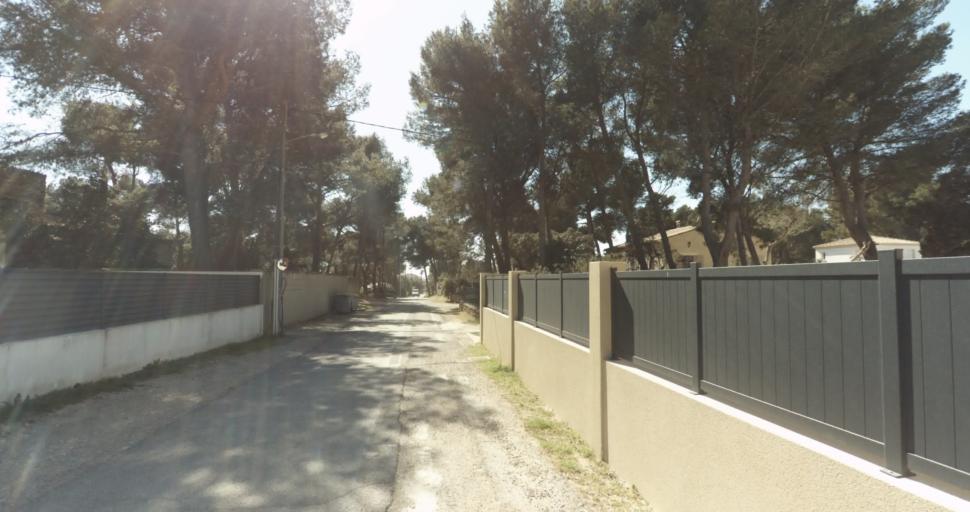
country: FR
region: Provence-Alpes-Cote d'Azur
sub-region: Departement des Bouches-du-Rhone
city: Pelissanne
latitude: 43.6383
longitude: 5.1632
